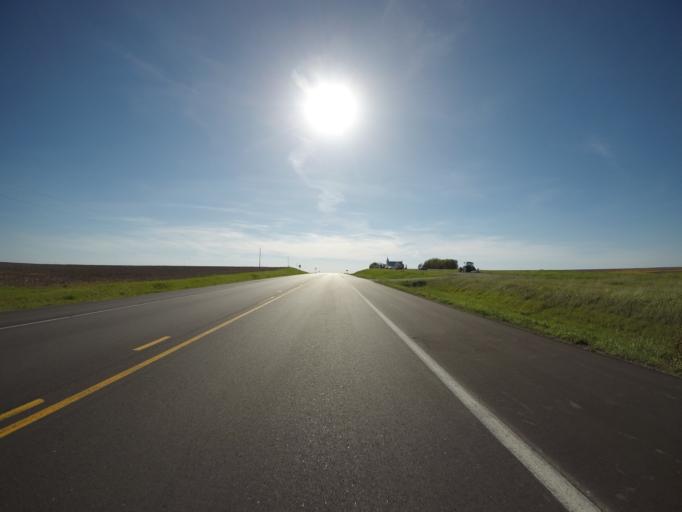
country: US
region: Kansas
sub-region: Clay County
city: Clay Center
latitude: 39.3796
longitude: -96.9949
